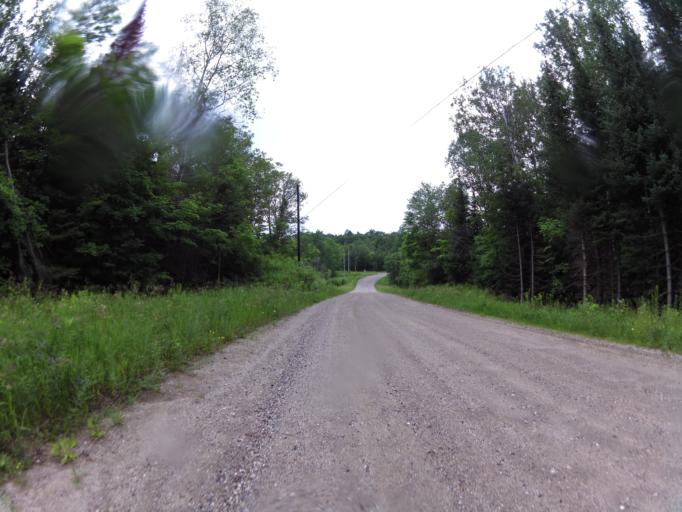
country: CA
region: Ontario
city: Renfrew
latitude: 45.0660
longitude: -76.7604
